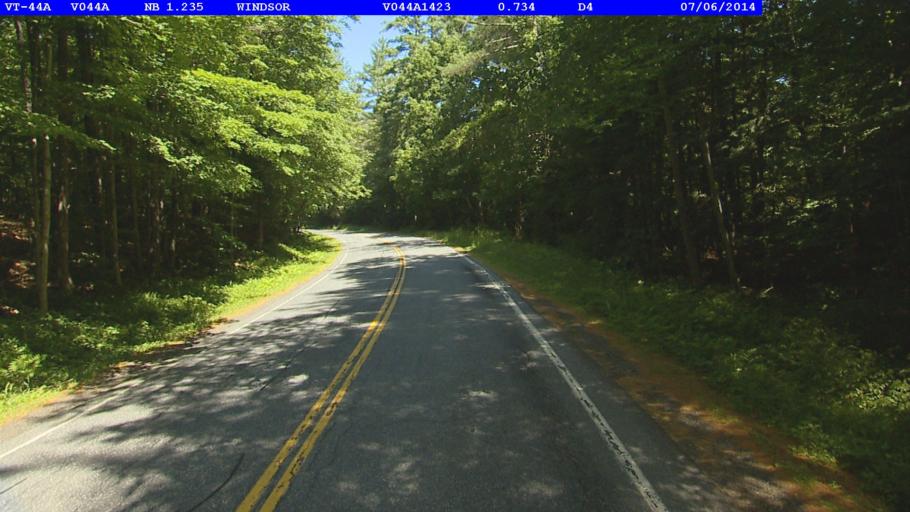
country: US
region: Vermont
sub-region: Windsor County
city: Windsor
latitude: 43.4389
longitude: -72.4062
